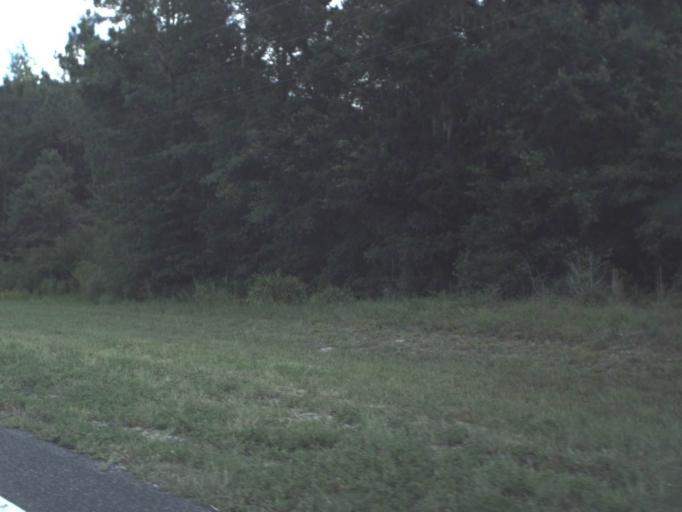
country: US
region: Florida
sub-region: Taylor County
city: Perry
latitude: 30.0393
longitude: -83.5473
